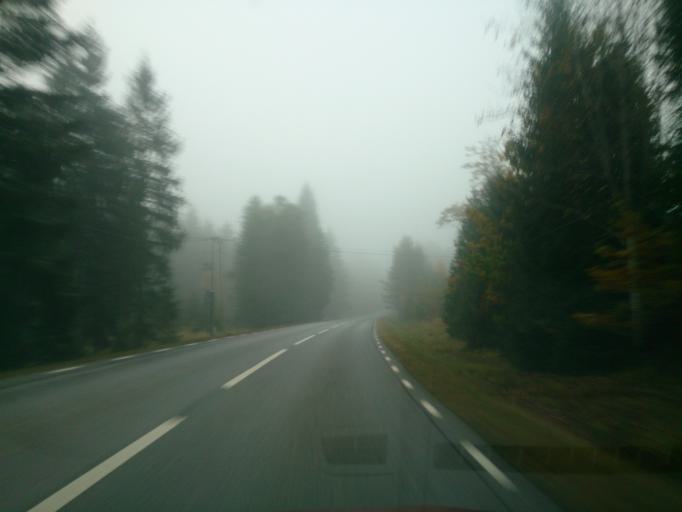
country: SE
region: OEstergoetland
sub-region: Atvidabergs Kommun
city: Atvidaberg
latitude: 58.1465
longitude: 15.9613
